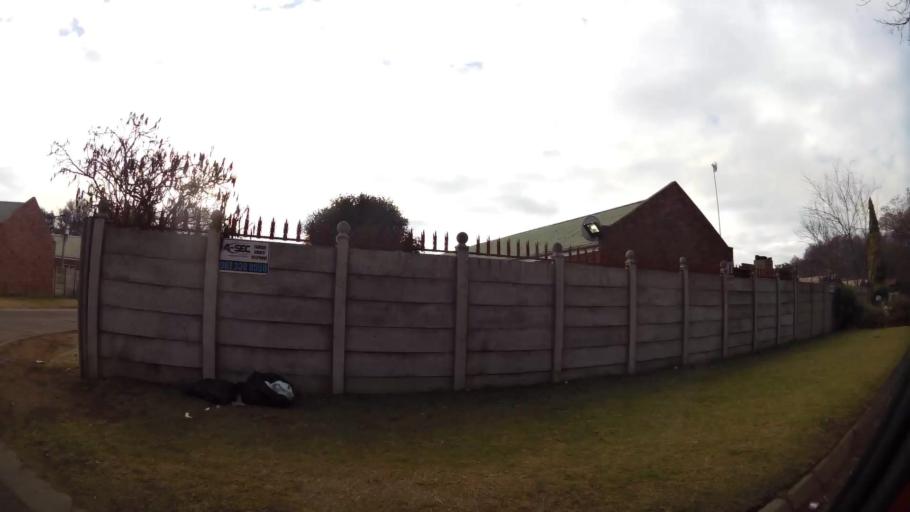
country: ZA
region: Gauteng
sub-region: Sedibeng District Municipality
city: Vanderbijlpark
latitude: -26.6830
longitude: 27.8147
